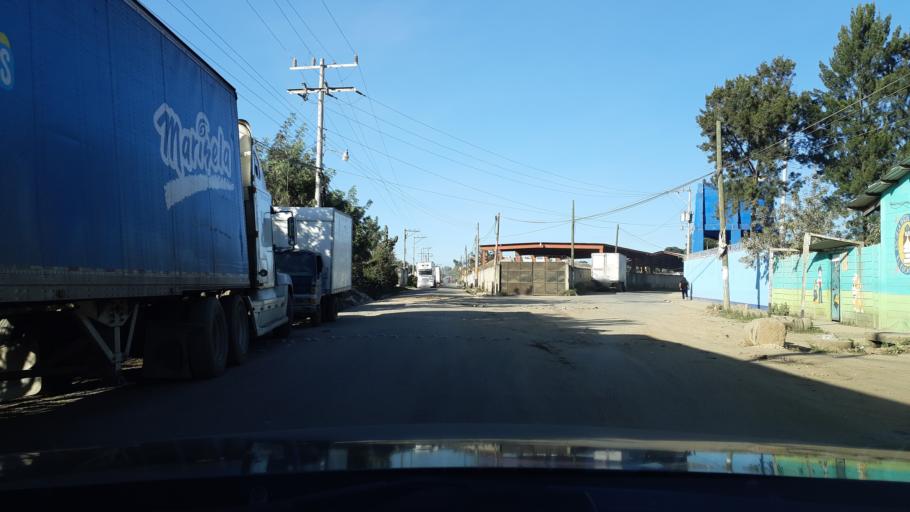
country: GT
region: Chimaltenango
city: El Tejar
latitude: 14.6415
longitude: -90.7992
